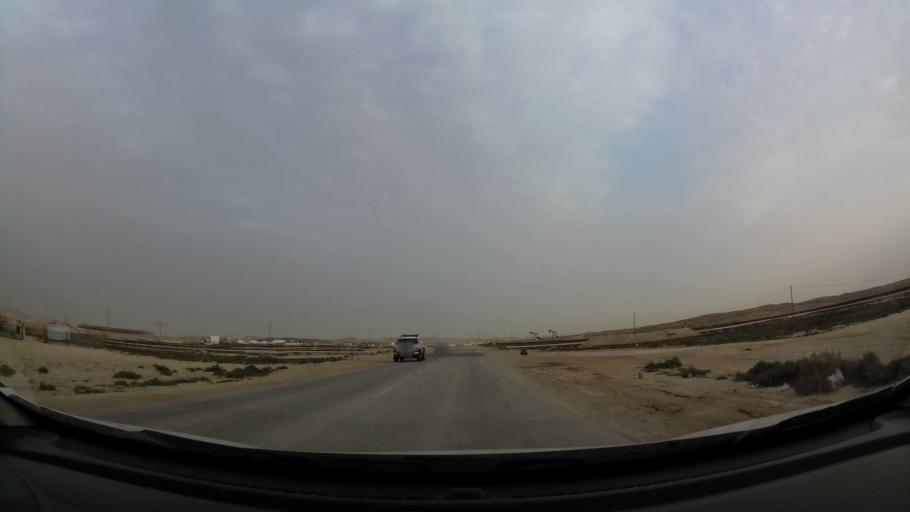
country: BH
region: Central Governorate
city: Dar Kulayb
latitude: 26.0159
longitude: 50.5765
